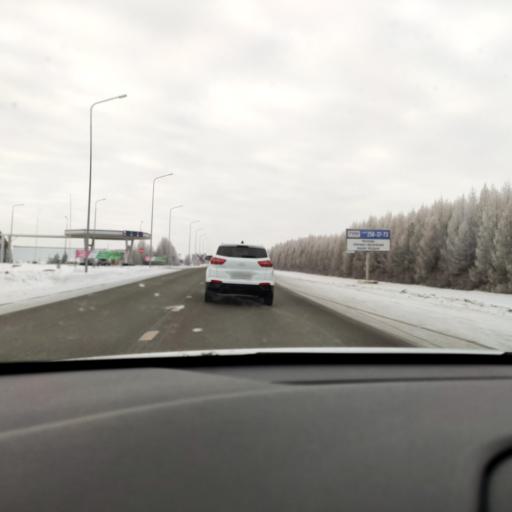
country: RU
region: Tatarstan
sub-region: Arskiy Rayon
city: Arsk
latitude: 56.1059
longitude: 49.8874
